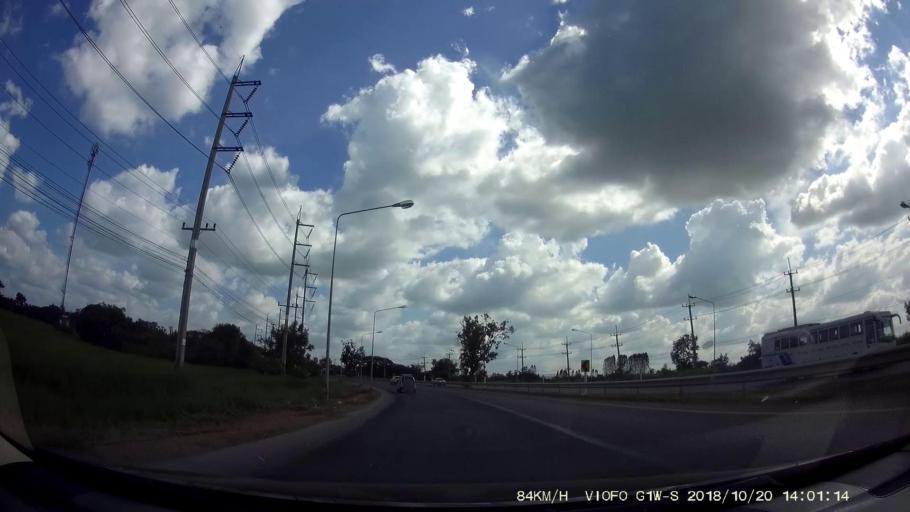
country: TH
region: Khon Kaen
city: Chum Phae
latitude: 16.5042
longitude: 102.1190
